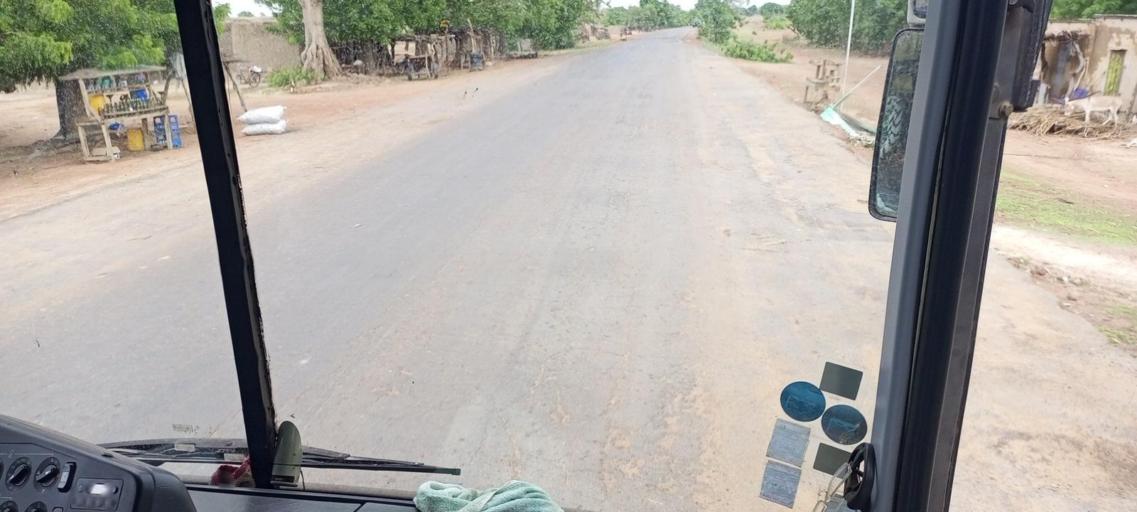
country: ML
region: Segou
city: Bla
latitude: 12.7353
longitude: -5.7262
